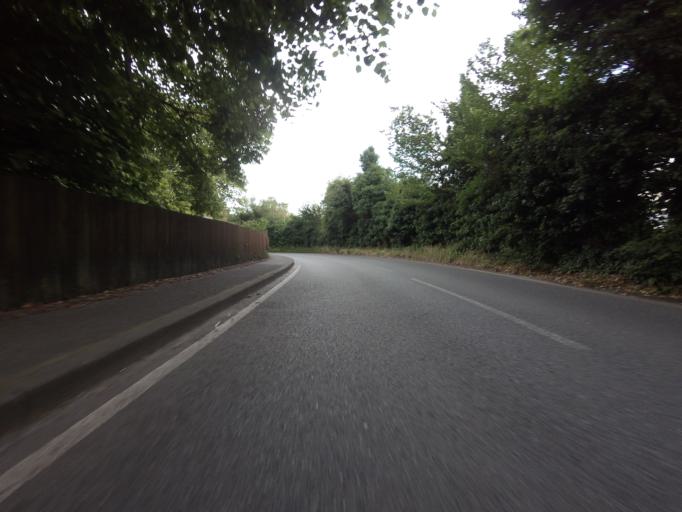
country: GB
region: England
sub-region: Greater London
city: Sidcup
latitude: 51.4214
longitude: 0.1208
